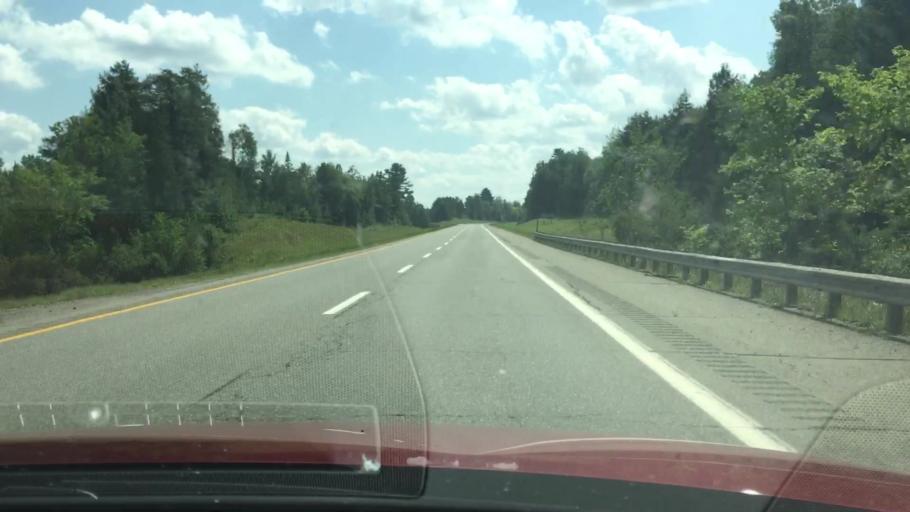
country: US
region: Maine
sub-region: Penobscot County
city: Lincoln
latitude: 45.3625
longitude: -68.6061
